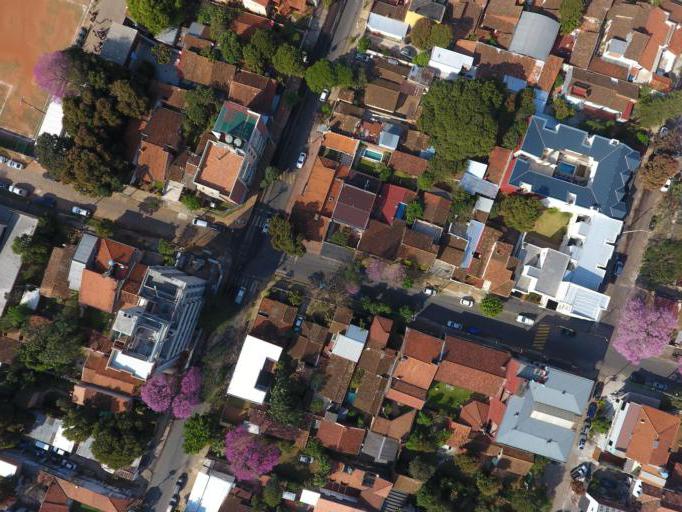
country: PY
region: Asuncion
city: Asuncion
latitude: -25.3083
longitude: -57.6072
